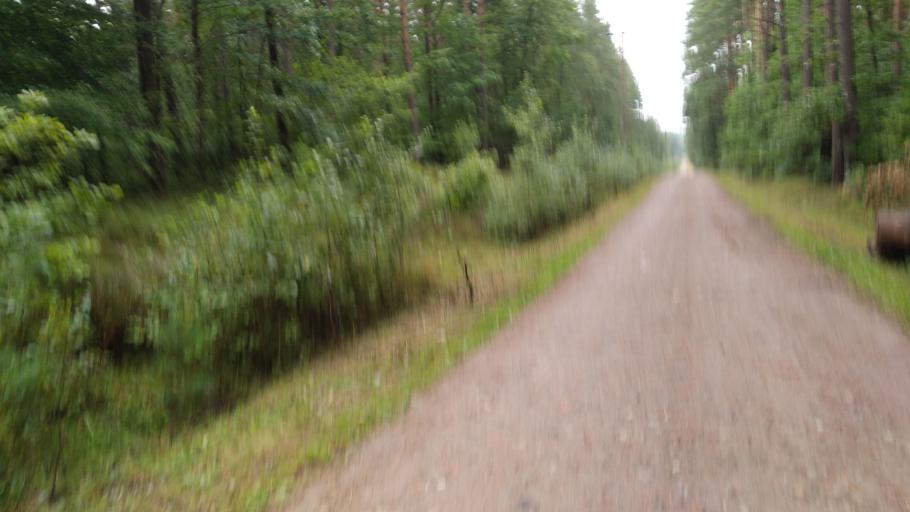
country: PL
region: Pomeranian Voivodeship
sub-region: Powiat wejherowski
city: Goscicino
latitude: 54.6190
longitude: 18.1554
